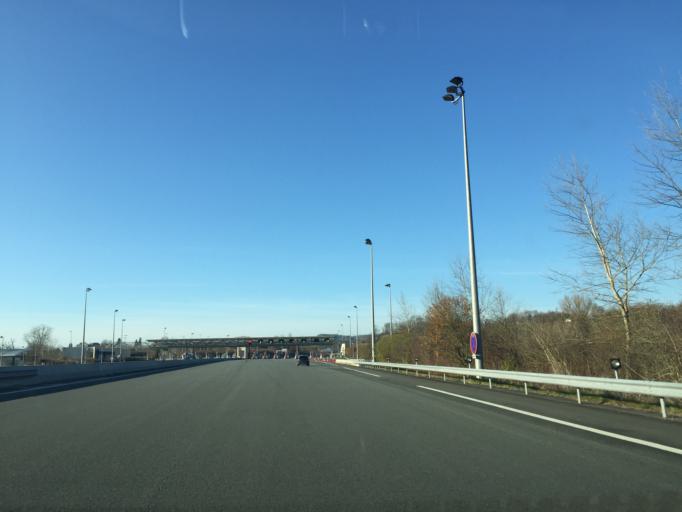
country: FR
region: Aquitaine
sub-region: Departement de la Dordogne
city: Montignac
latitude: 45.1501
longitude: 1.1709
